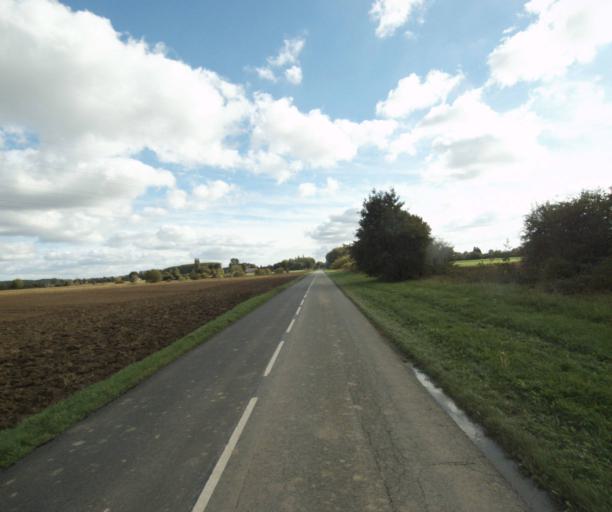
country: FR
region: Nord-Pas-de-Calais
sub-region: Departement du Nord
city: Bois-Grenier
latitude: 50.6608
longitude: 2.9018
